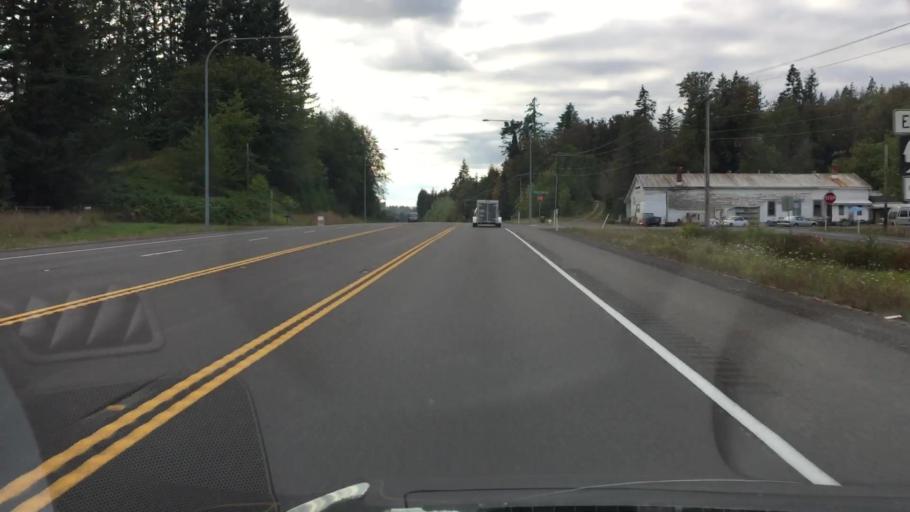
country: US
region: Washington
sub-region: Lewis County
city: Napavine
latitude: 46.5250
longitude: -122.5948
